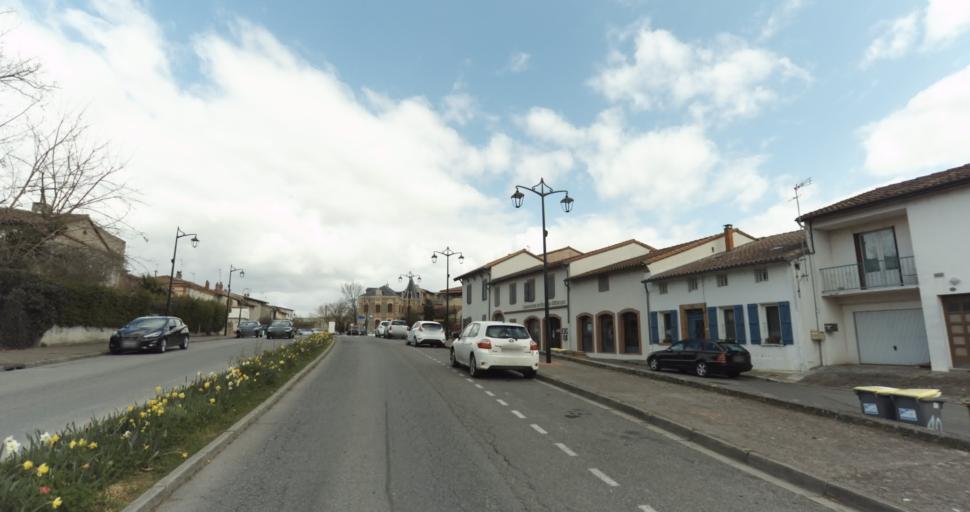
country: FR
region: Midi-Pyrenees
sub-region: Departement de la Haute-Garonne
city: Auterive
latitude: 43.3512
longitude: 1.4791
